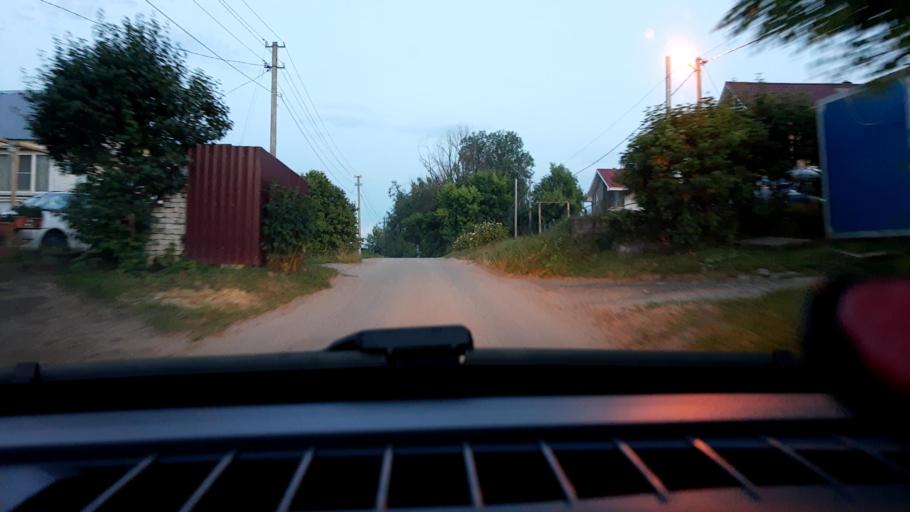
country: RU
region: Nizjnij Novgorod
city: Afonino
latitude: 56.2509
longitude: 44.0775
